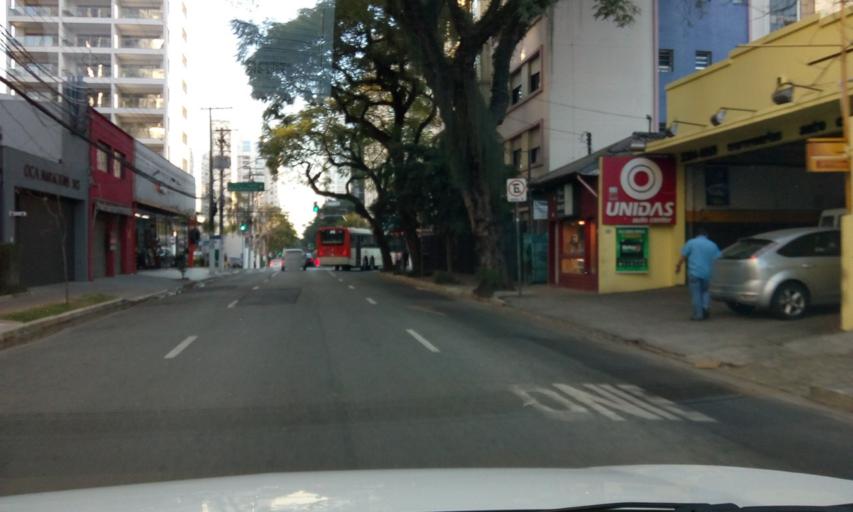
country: BR
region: Sao Paulo
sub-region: Sao Paulo
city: Sao Paulo
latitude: -23.6041
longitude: -46.6581
